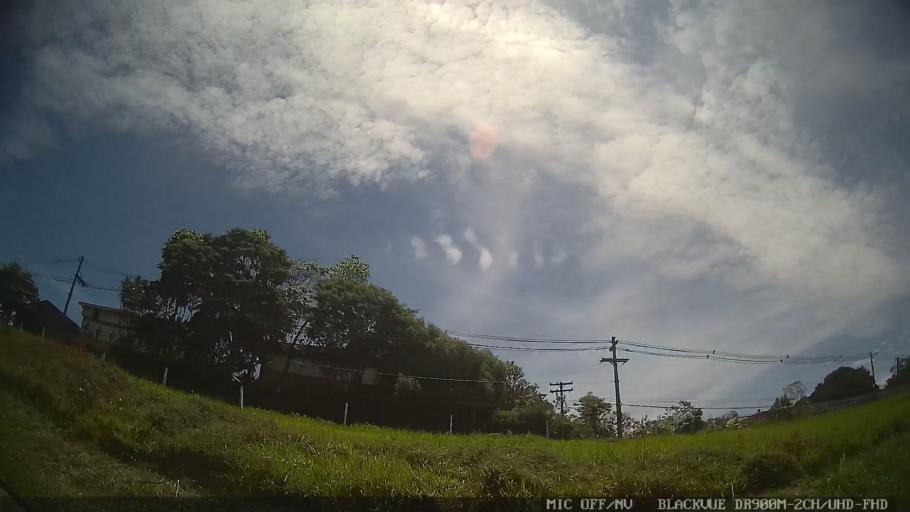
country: BR
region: Sao Paulo
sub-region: Valinhos
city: Valinhos
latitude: -23.0075
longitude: -47.0271
